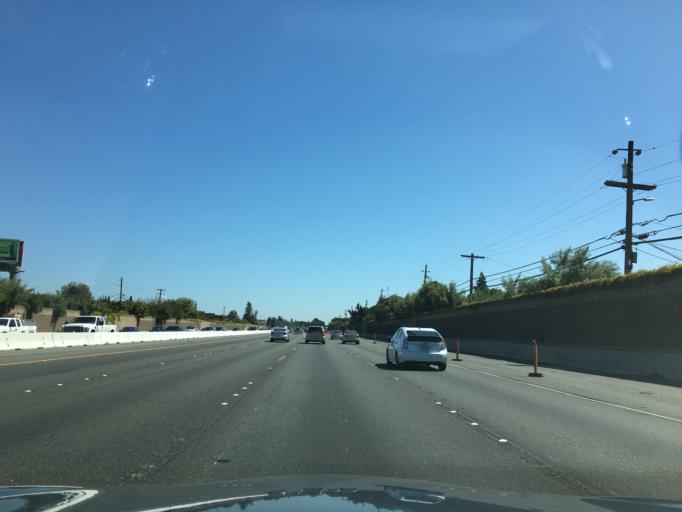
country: US
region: California
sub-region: San Mateo County
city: East Palo Alto
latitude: 37.4562
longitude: -122.1340
